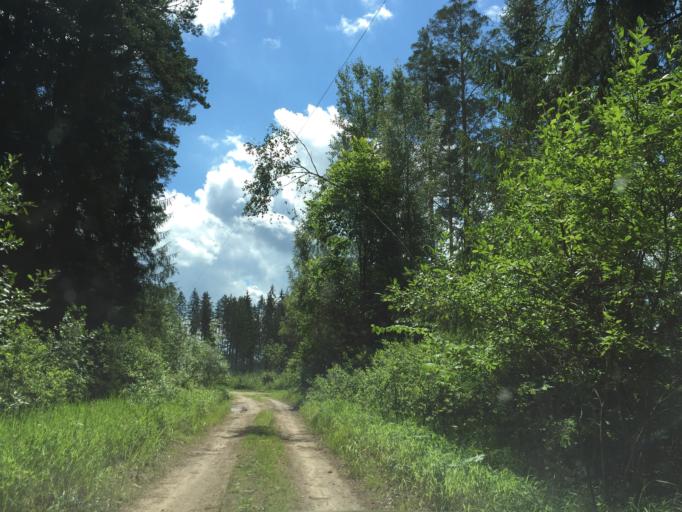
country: LV
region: Ropazu
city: Ropazi
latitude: 56.8979
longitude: 24.7158
